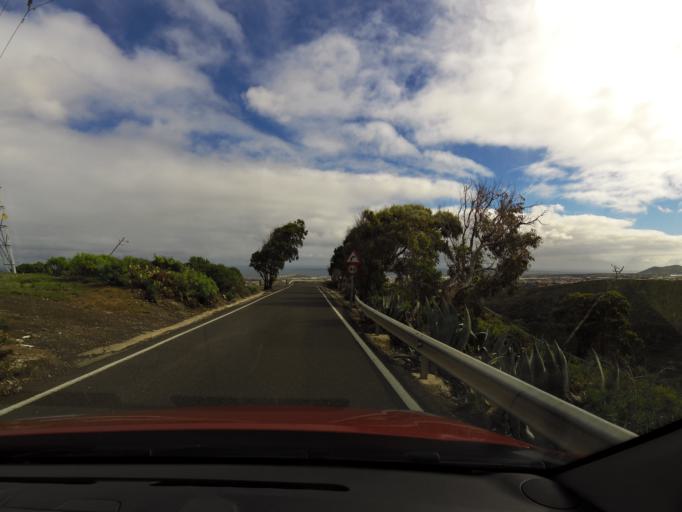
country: ES
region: Canary Islands
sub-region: Provincia de Las Palmas
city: Telde
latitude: 28.0123
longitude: -15.4363
